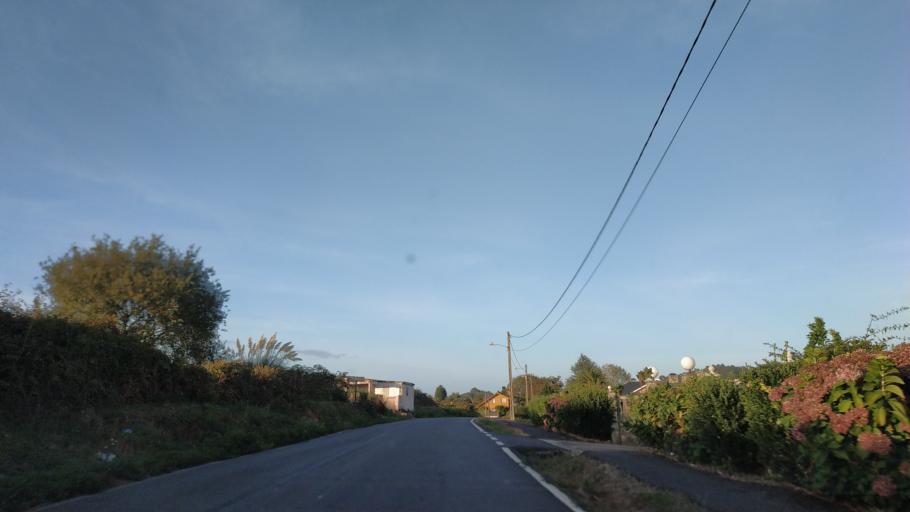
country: ES
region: Galicia
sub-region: Provincia da Coruna
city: Oleiros
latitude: 43.3584
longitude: -8.3434
